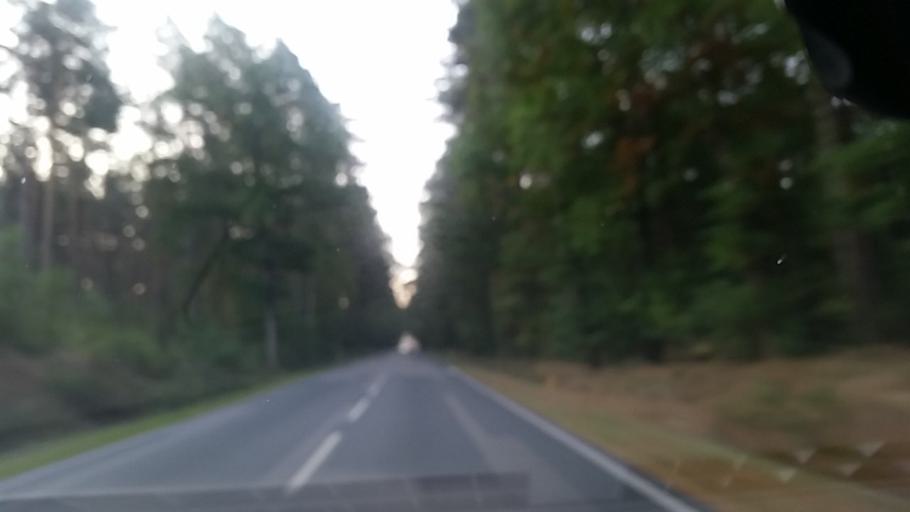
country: DE
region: Lower Saxony
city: Tulau
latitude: 52.6323
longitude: 10.8114
